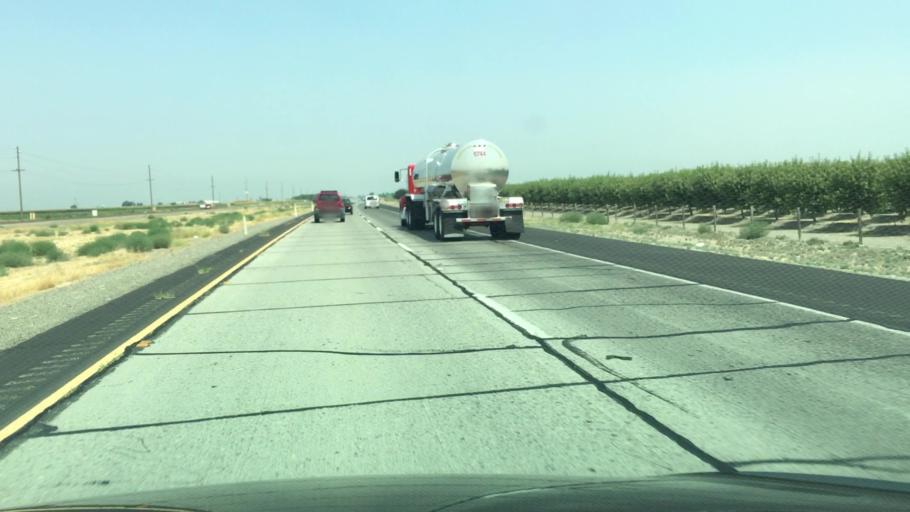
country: US
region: California
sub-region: Merced County
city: Dos Palos
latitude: 37.0542
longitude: -120.6966
